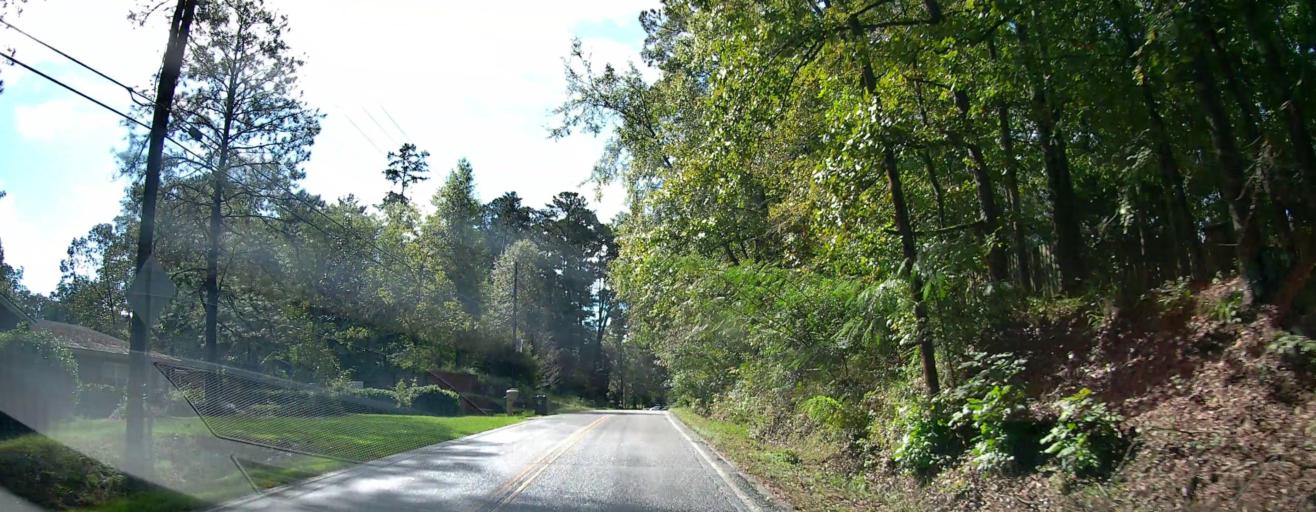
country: US
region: Georgia
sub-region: Bibb County
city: Macon
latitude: 32.9084
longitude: -83.7168
